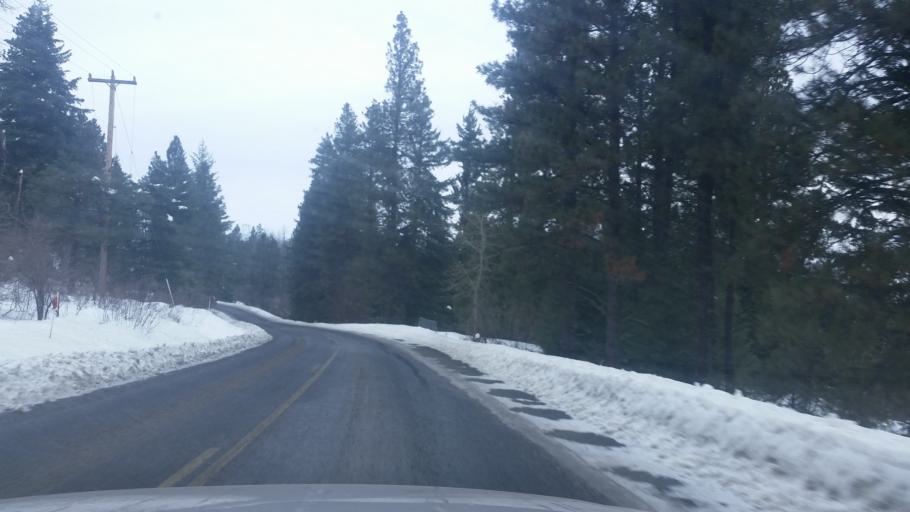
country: US
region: Washington
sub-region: Kittitas County
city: Cle Elum
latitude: 47.1481
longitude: -120.8148
